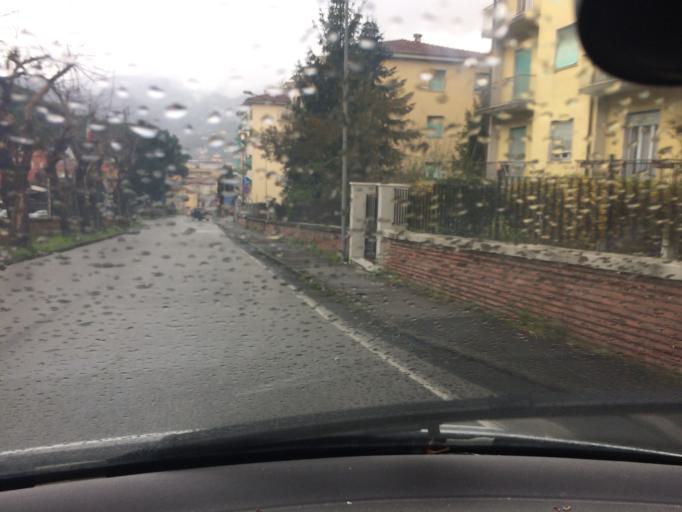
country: IT
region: Tuscany
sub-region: Provincia di Massa-Carrara
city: Carrara
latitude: 44.0745
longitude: 10.1055
